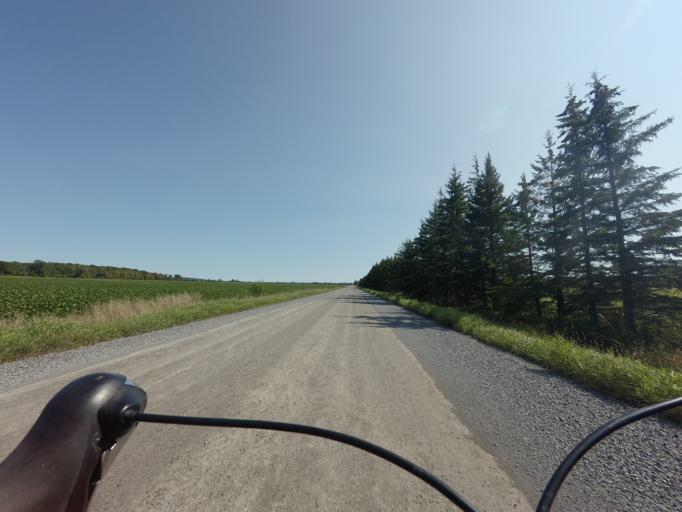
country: CA
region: Ontario
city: Arnprior
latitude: 45.3819
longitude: -76.1528
